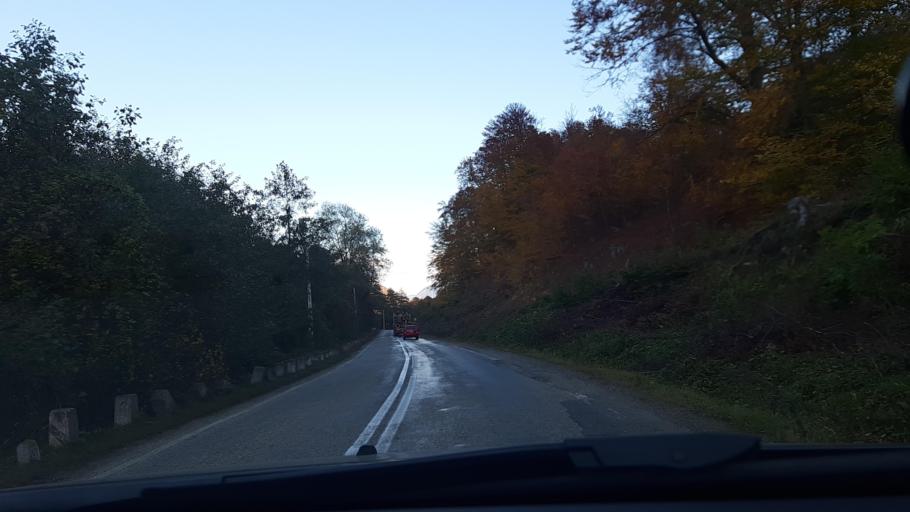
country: RO
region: Valcea
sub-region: Comuna Brezoi
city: Brezoi
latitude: 45.3471
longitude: 24.1614
